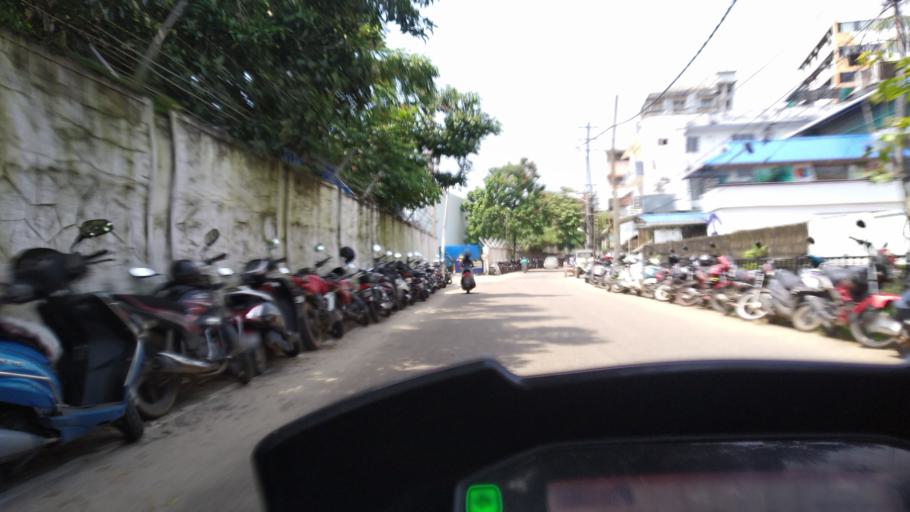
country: IN
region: Kerala
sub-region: Ernakulam
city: Cochin
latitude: 9.9600
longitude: 76.2873
